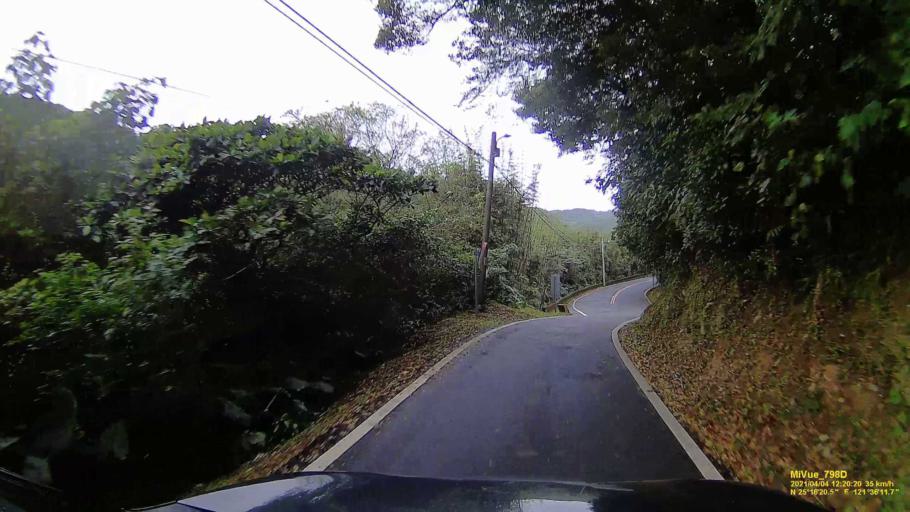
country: TW
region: Taiwan
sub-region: Keelung
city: Keelung
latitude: 25.2726
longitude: 121.6031
